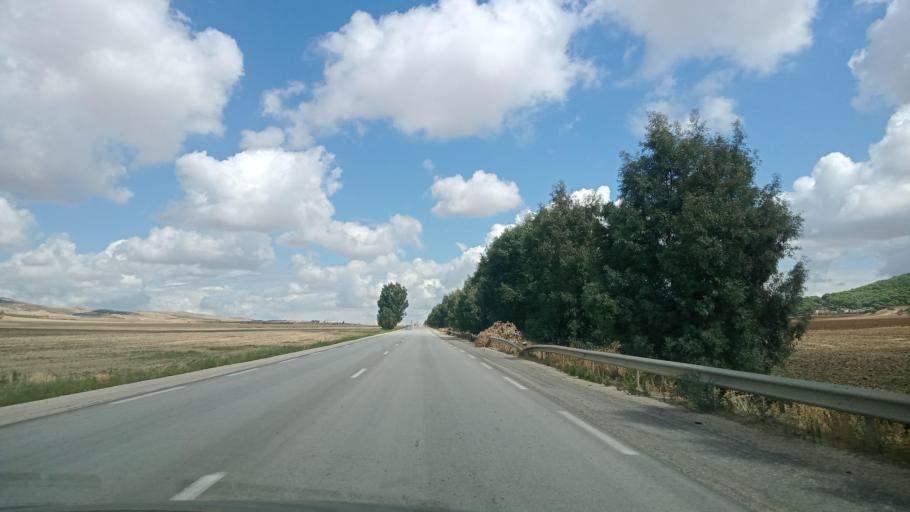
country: TN
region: Silyanah
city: Al Karib
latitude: 36.3108
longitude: 9.1015
